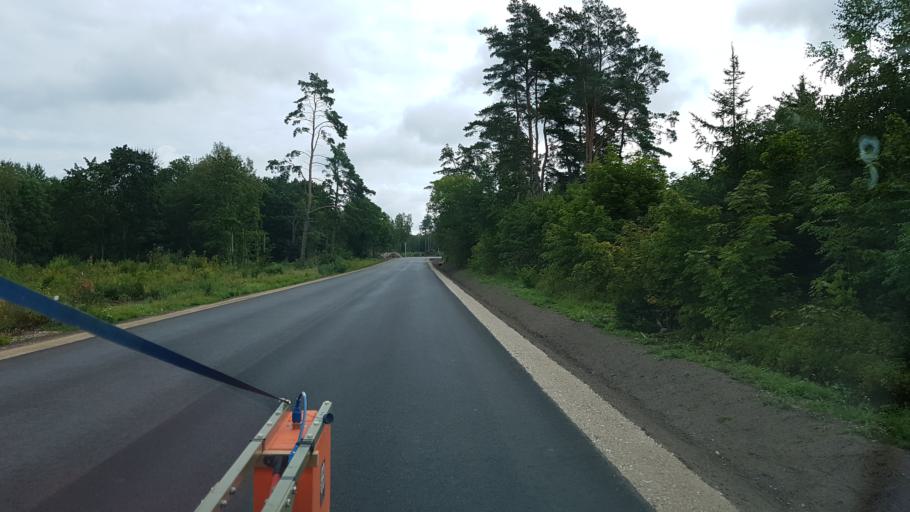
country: EE
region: Harju
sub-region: Nissi vald
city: Turba
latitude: 59.0995
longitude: 24.0062
